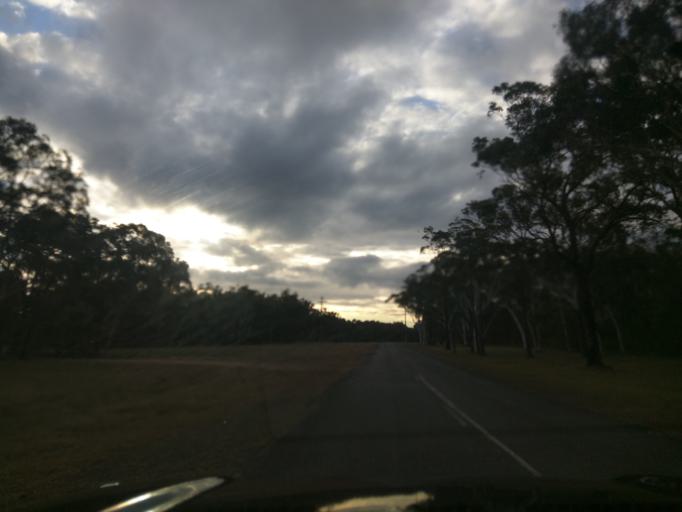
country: AU
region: New South Wales
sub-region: Wollondilly
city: Douglas Park
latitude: -34.3209
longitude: 150.7444
